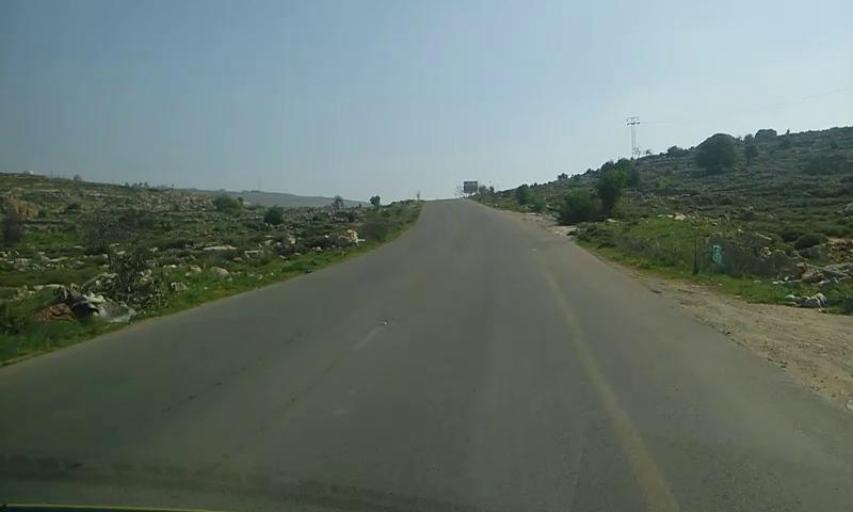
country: PS
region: West Bank
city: Silwad
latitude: 31.9696
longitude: 35.2763
